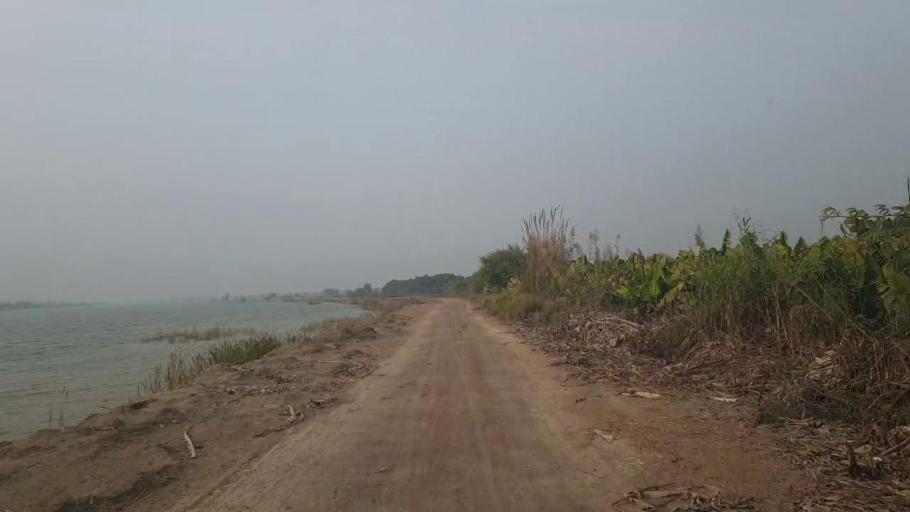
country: PK
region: Sindh
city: Berani
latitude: 25.8121
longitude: 68.7398
